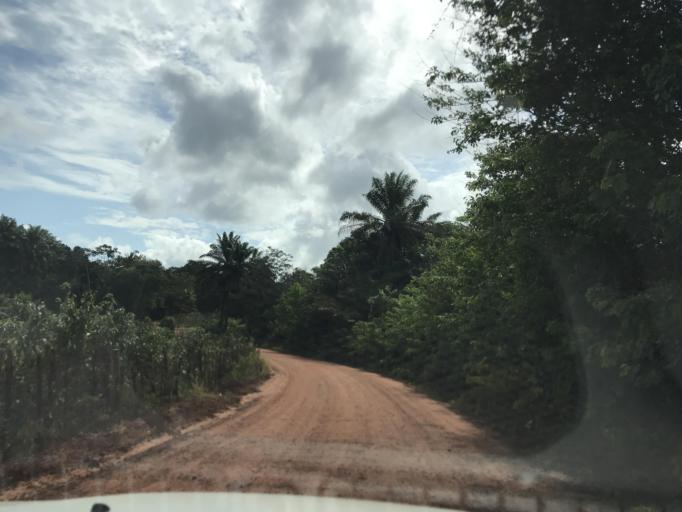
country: BR
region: Bahia
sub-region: Entre Rios
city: Entre Rios
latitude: -12.1722
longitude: -38.1425
